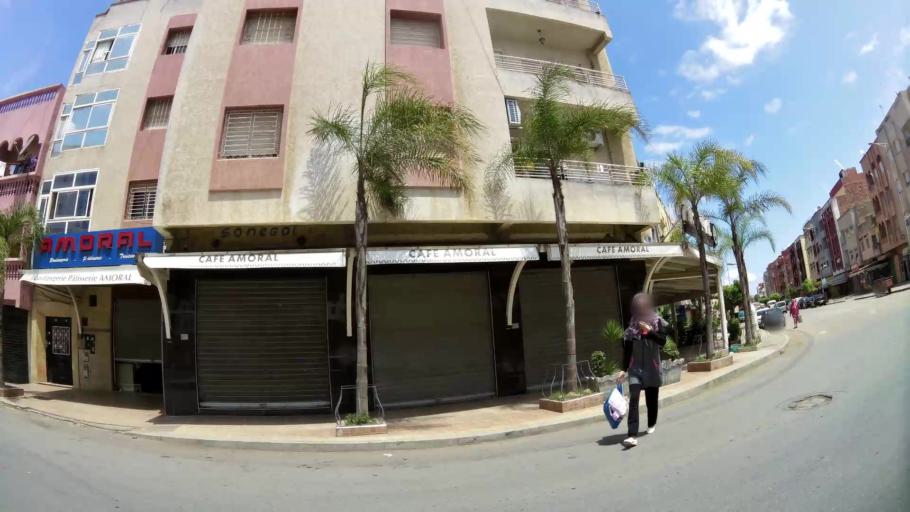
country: MA
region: Gharb-Chrarda-Beni Hssen
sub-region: Kenitra Province
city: Kenitra
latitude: 34.2676
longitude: -6.6022
